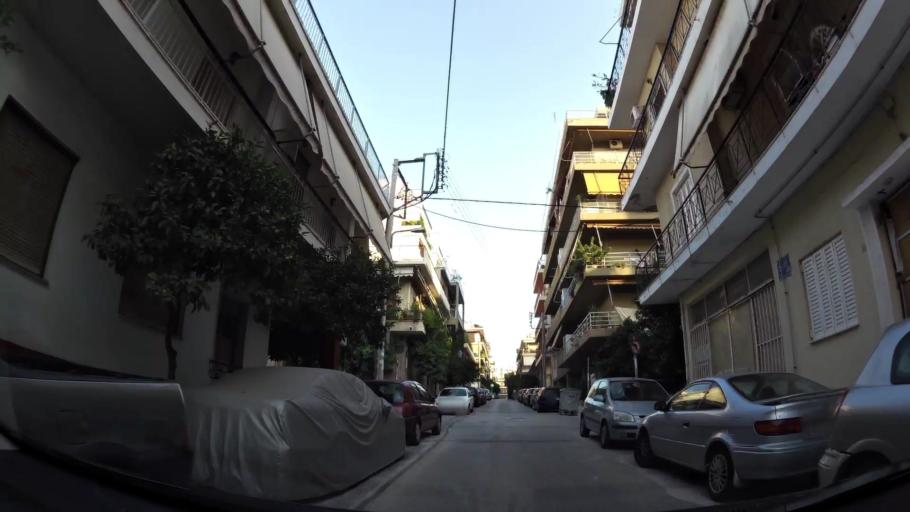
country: GR
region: Attica
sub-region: Nomarchia Athinas
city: Galatsi
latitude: 38.0244
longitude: 23.7478
